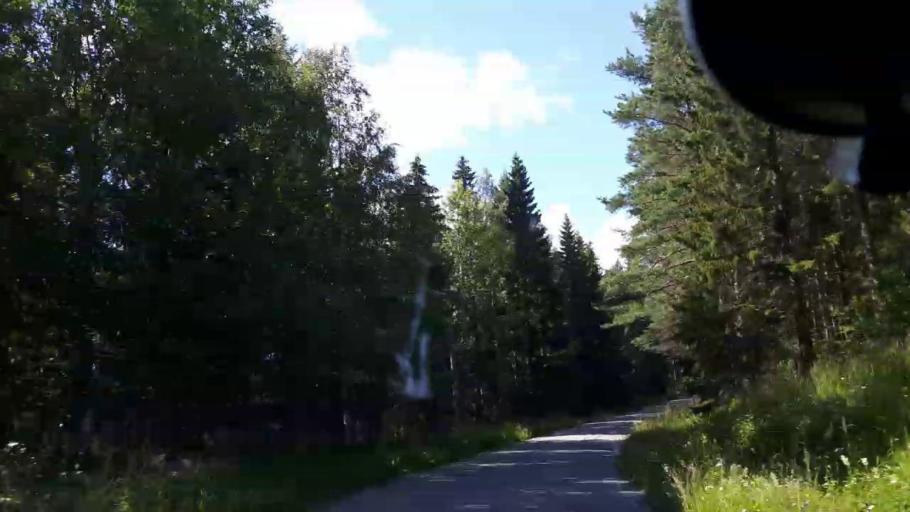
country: SE
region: Jaemtland
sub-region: Braecke Kommun
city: Braecke
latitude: 62.8579
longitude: 15.2785
